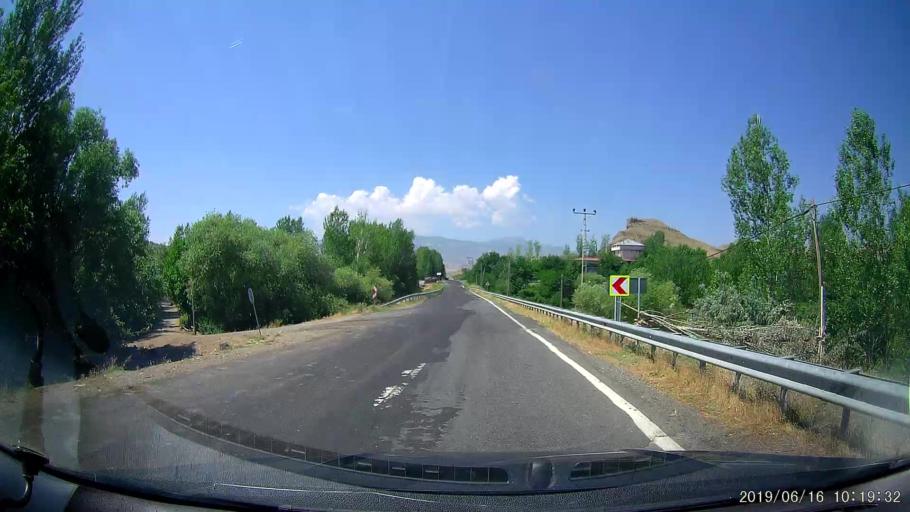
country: TR
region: Igdir
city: Tuzluca
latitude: 40.1545
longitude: 43.6555
